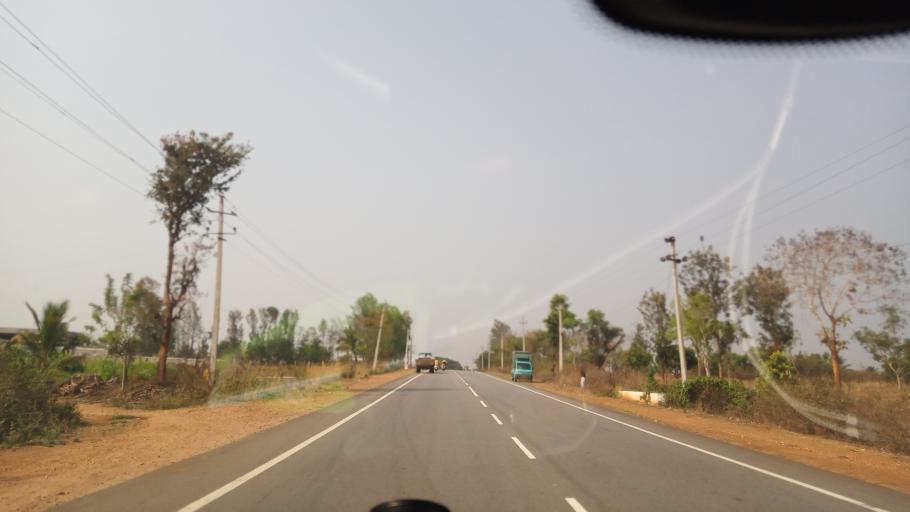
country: IN
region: Karnataka
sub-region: Mandya
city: Melukote
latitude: 12.6970
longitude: 76.6977
